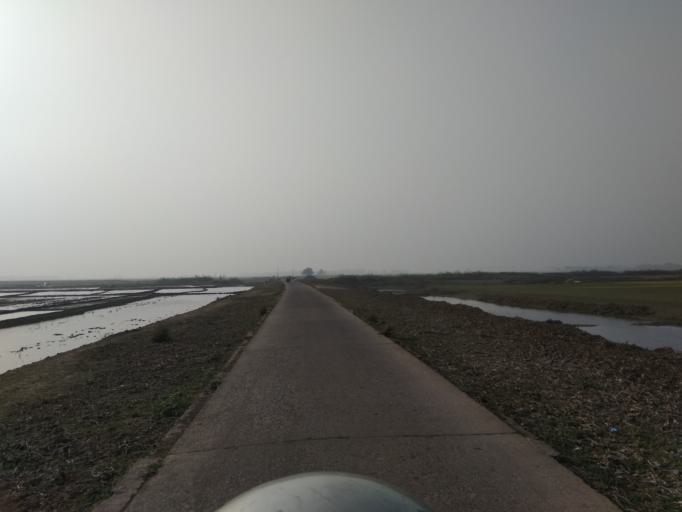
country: BD
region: Rajshahi
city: Ishurdi
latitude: 24.4831
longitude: 89.2237
